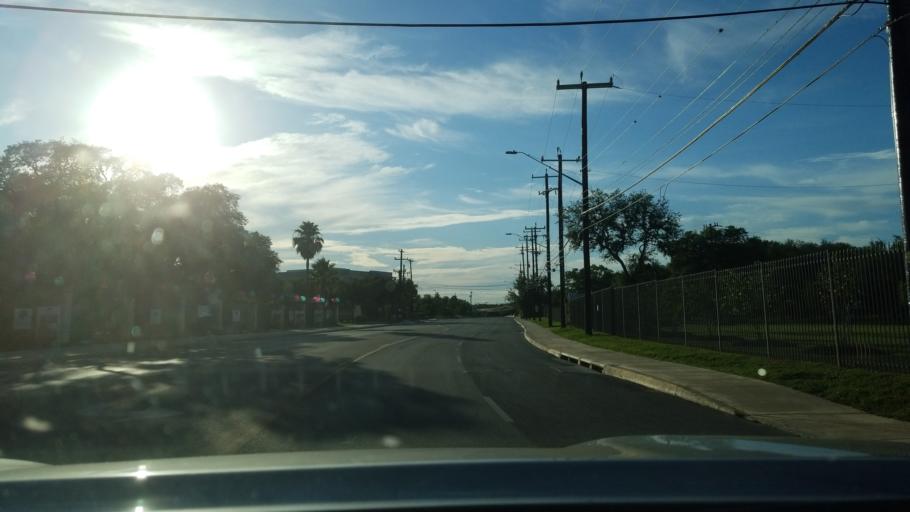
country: US
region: Texas
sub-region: Bexar County
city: Hollywood Park
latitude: 29.6166
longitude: -98.4549
